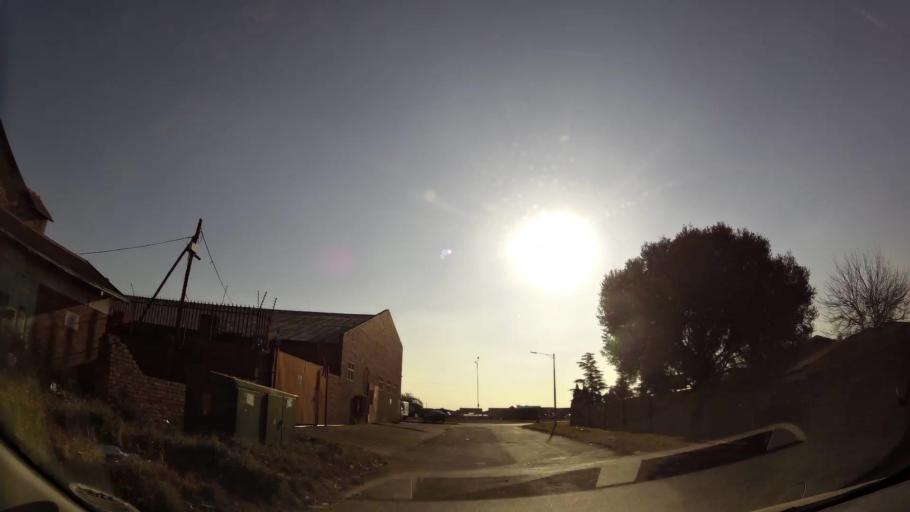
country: ZA
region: Gauteng
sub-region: West Rand District Municipality
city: Randfontein
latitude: -26.1942
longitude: 27.7010
